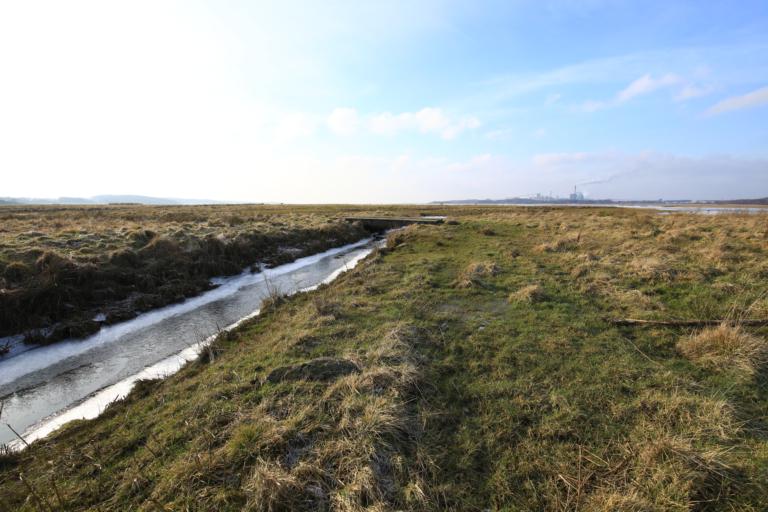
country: SE
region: Halland
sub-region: Varbergs Kommun
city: Veddige
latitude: 57.2168
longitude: 12.2175
